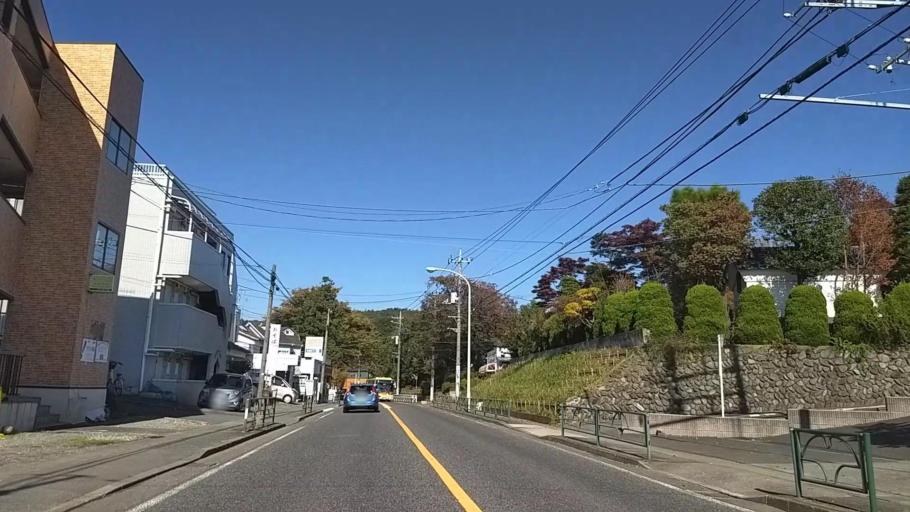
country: JP
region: Tokyo
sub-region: Machida-shi
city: Machida
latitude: 35.5825
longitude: 139.4038
